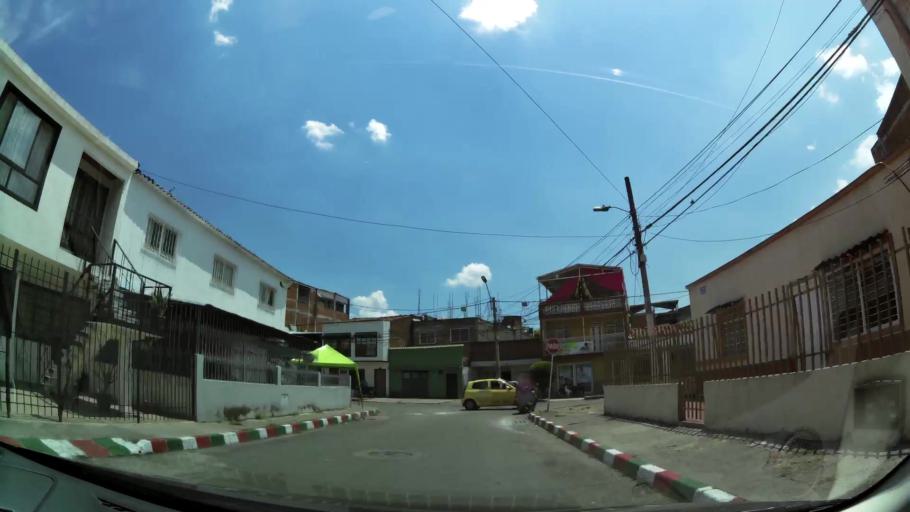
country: CO
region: Valle del Cauca
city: Cali
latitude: 3.4462
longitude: -76.5027
